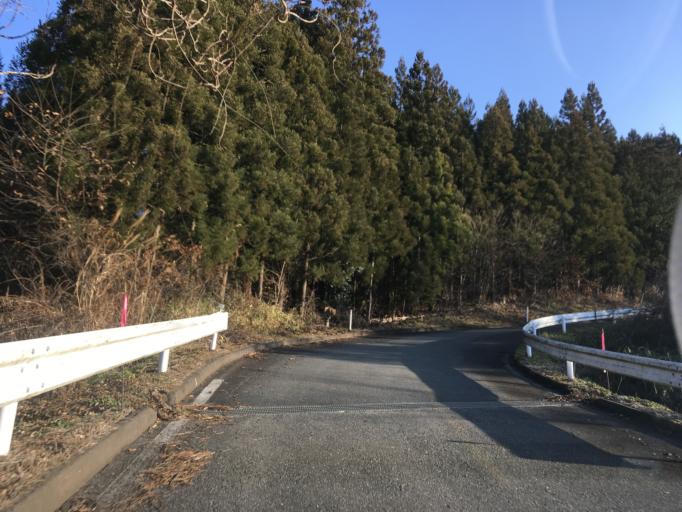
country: JP
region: Iwate
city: Ichinoseki
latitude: 38.8265
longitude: 141.2587
